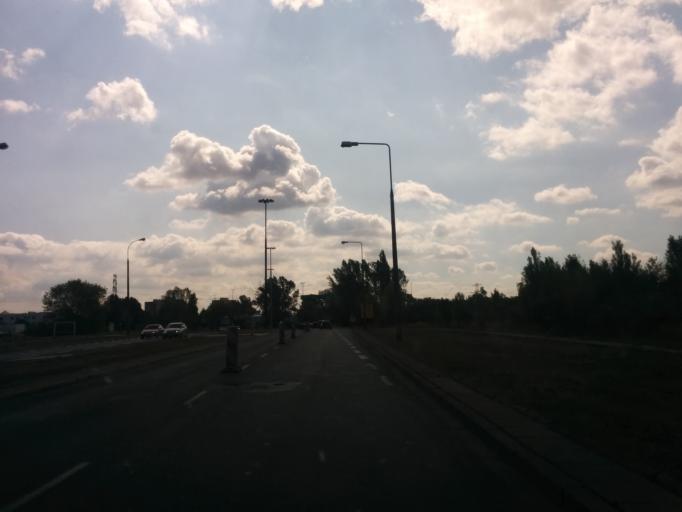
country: PL
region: Masovian Voivodeship
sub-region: Warszawa
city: Targowek
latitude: 52.2995
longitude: 21.0123
